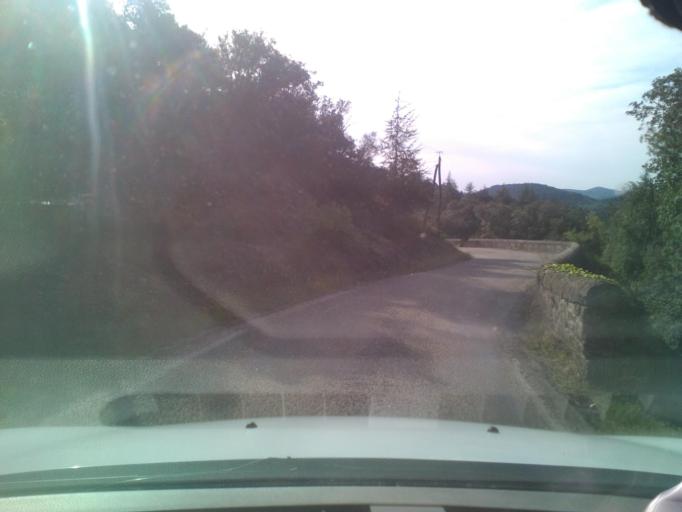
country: FR
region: Languedoc-Roussillon
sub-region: Departement du Gard
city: Lasalle
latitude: 44.0732
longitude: 3.8293
